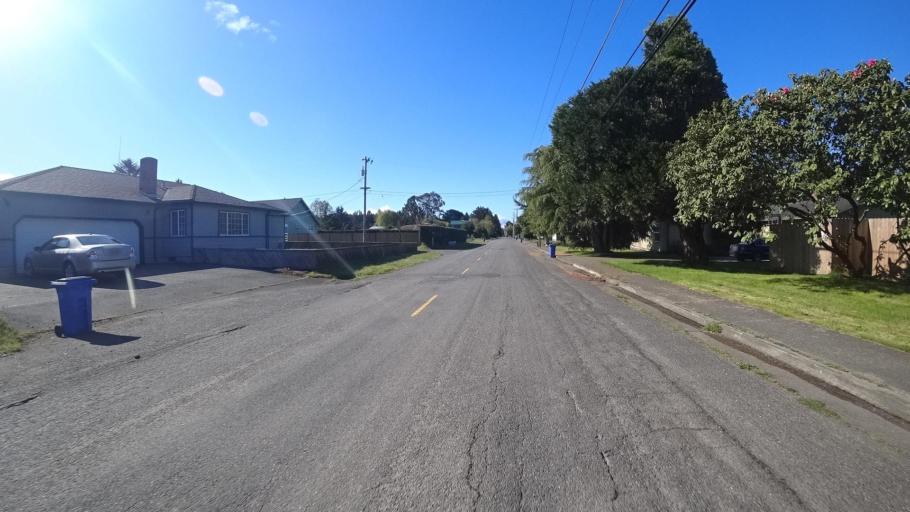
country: US
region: California
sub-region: Humboldt County
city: McKinleyville
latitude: 40.9735
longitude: -124.0959
